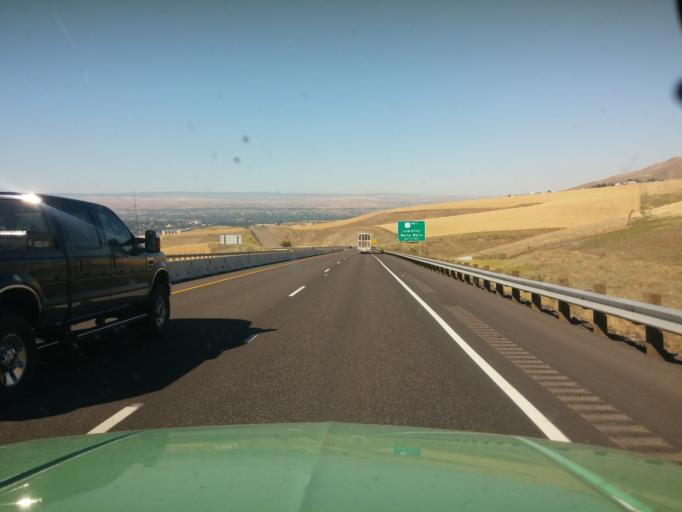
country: US
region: Idaho
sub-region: Nez Perce County
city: Lewiston
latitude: 46.4459
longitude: -116.9786
